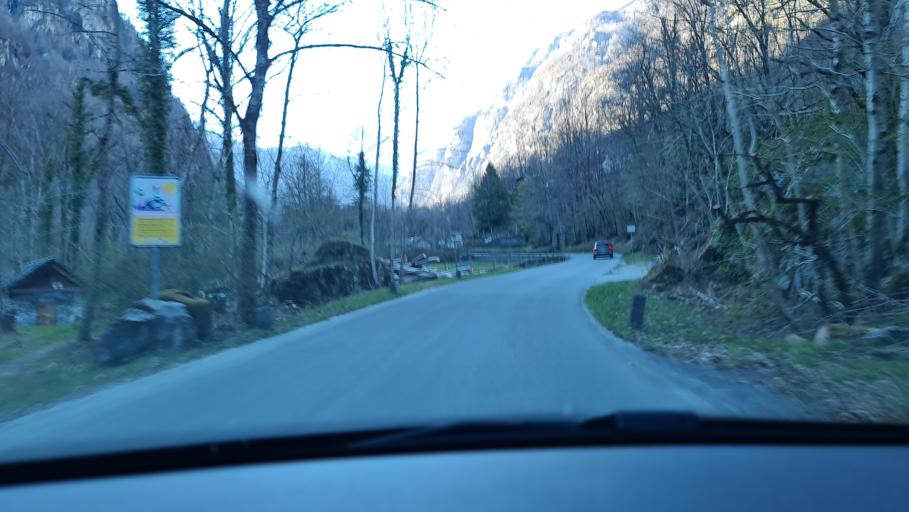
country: CH
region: Ticino
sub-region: Vallemaggia District
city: Cevio
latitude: 46.3557
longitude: 8.5848
